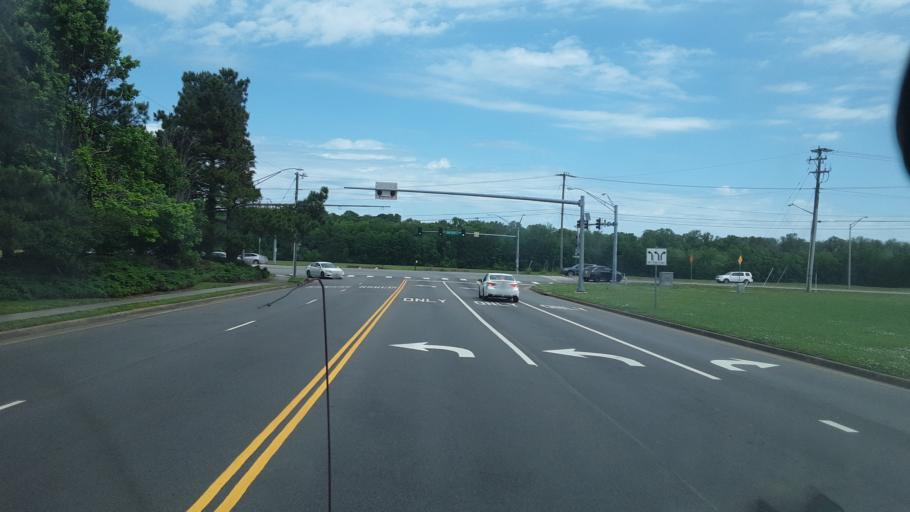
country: US
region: Virginia
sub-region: City of Virginia Beach
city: Virginia Beach
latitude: 36.7851
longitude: -75.9932
